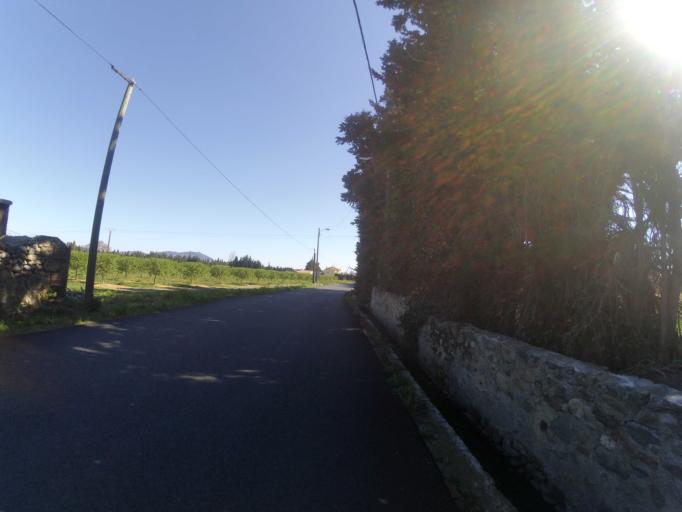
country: FR
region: Languedoc-Roussillon
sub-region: Departement des Pyrenees-Orientales
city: Ille-sur-Tet
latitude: 42.6674
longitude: 2.6424
